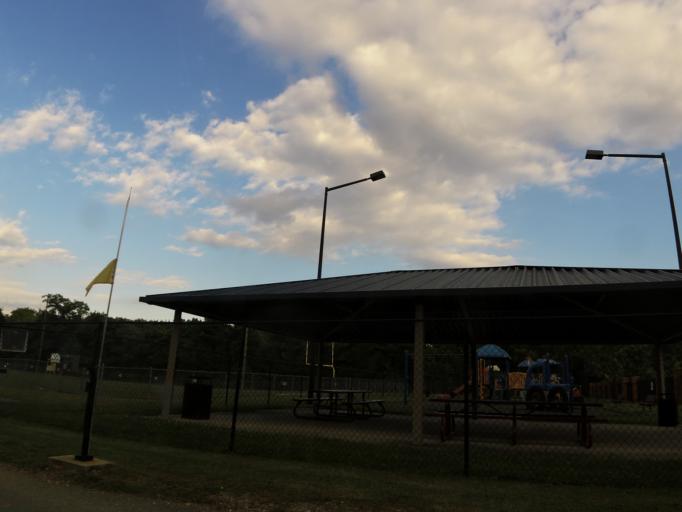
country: US
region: Tennessee
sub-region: Knox County
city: Knoxville
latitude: 35.9538
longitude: -83.9546
